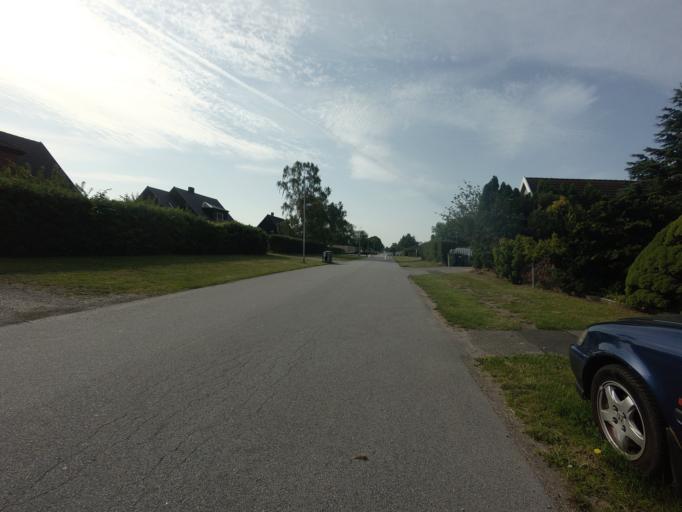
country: SE
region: Skane
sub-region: Vellinge Kommun
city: Vellinge
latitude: 55.4944
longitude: 13.0110
